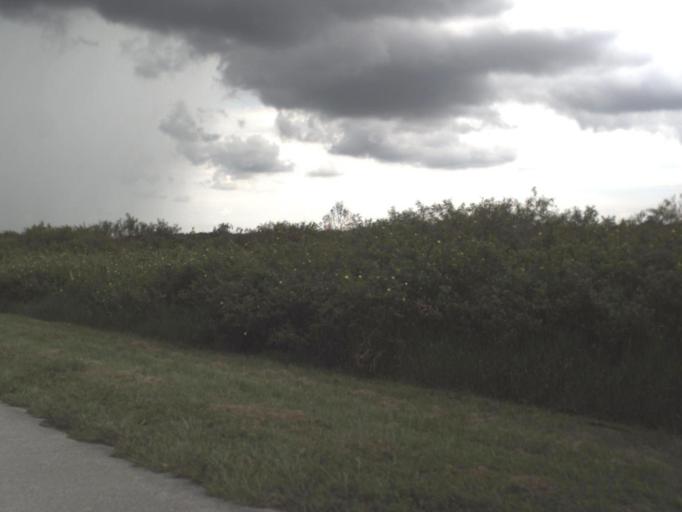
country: US
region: Florida
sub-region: Hendry County
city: Port LaBelle
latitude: 26.9114
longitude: -81.3273
